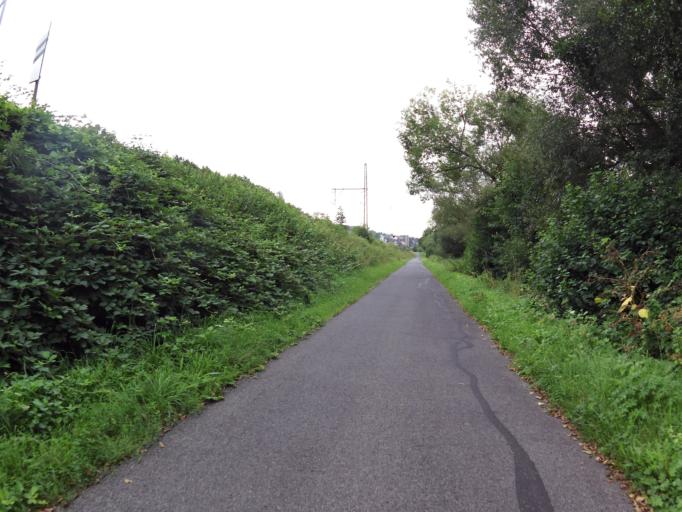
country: DE
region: Bavaria
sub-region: Regierungsbezirk Unterfranken
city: Schonungen
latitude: 50.0533
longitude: 10.2961
